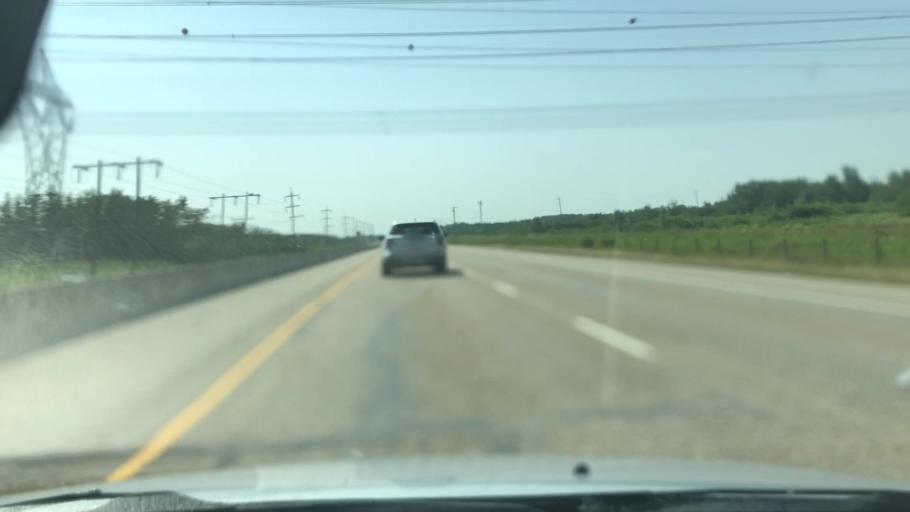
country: CA
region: Alberta
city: Devon
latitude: 53.4620
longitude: -113.7626
